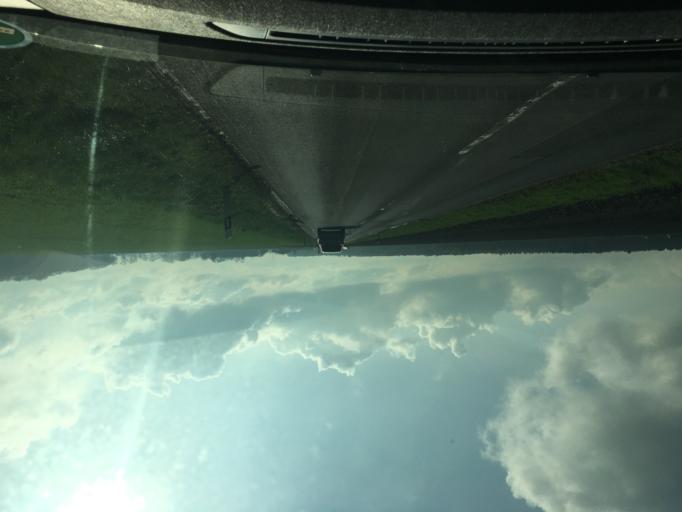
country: DE
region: North Rhine-Westphalia
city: Bornheim
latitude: 50.7350
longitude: 6.9477
